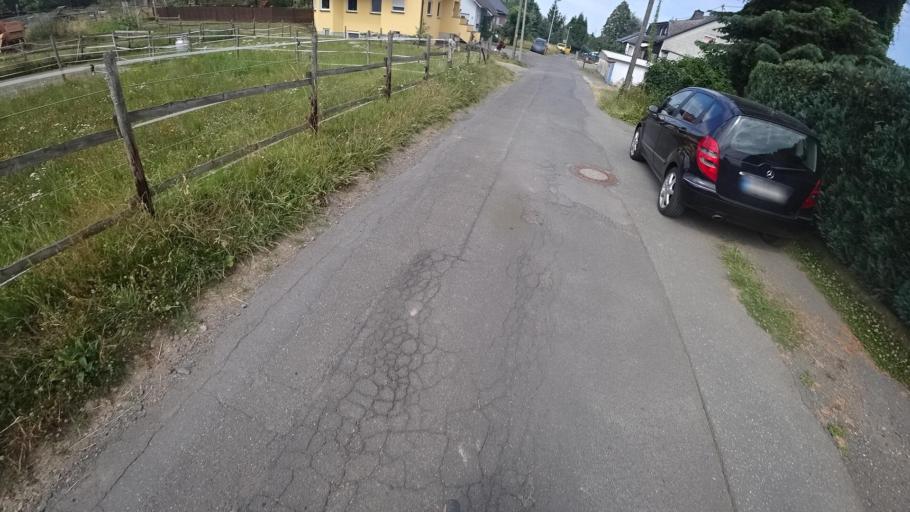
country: DE
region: Rheinland-Pfalz
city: Spessart
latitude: 50.4895
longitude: 7.0937
